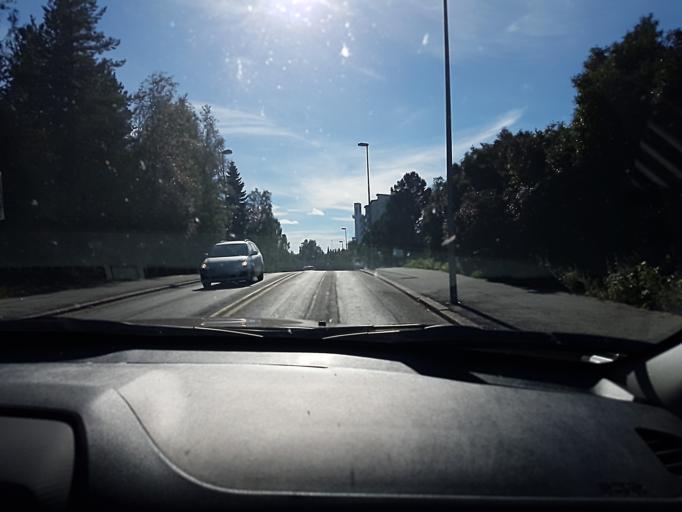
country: FI
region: Southern Ostrobothnia
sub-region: Seinaejoki
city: Seinaejoki
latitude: 62.7889
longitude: 22.8548
